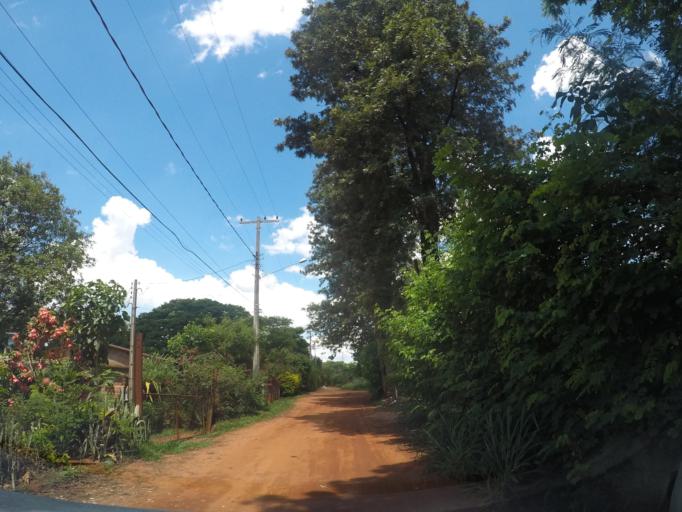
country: BR
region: Sao Paulo
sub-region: Sumare
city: Sumare
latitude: -22.8388
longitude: -47.2455
